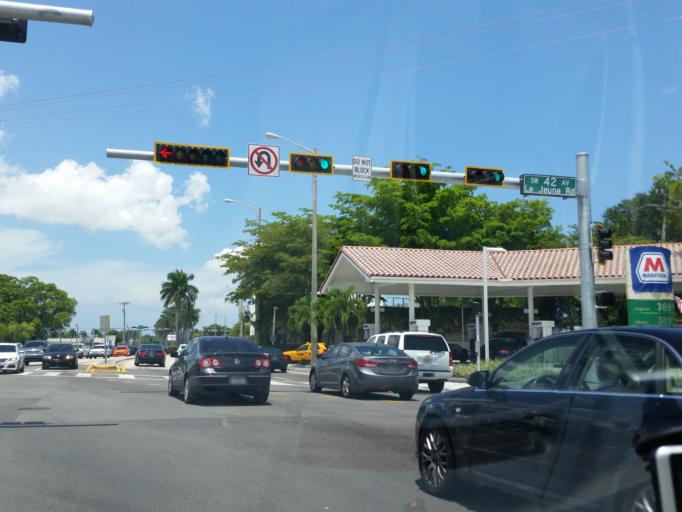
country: US
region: Florida
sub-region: Miami-Dade County
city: Coral Gables
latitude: 25.7264
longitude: -80.2618
